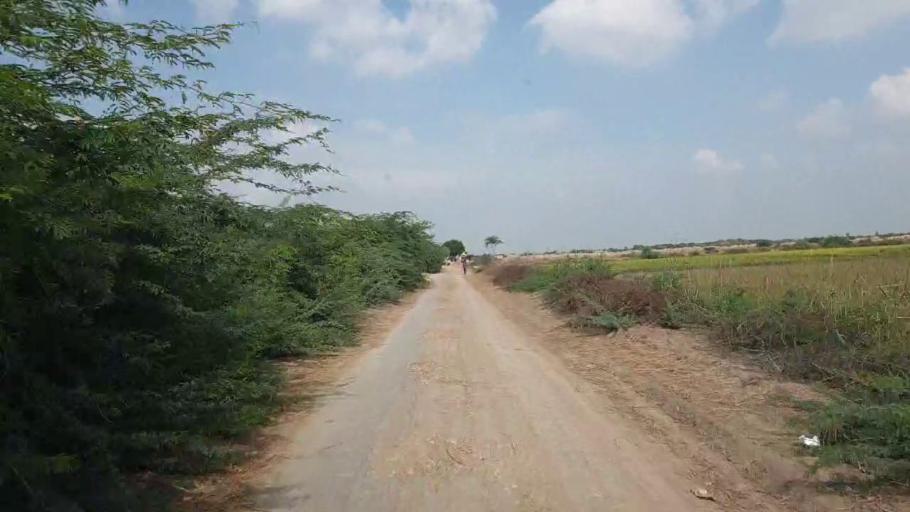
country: PK
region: Sindh
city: Badin
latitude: 24.4702
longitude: 68.5902
